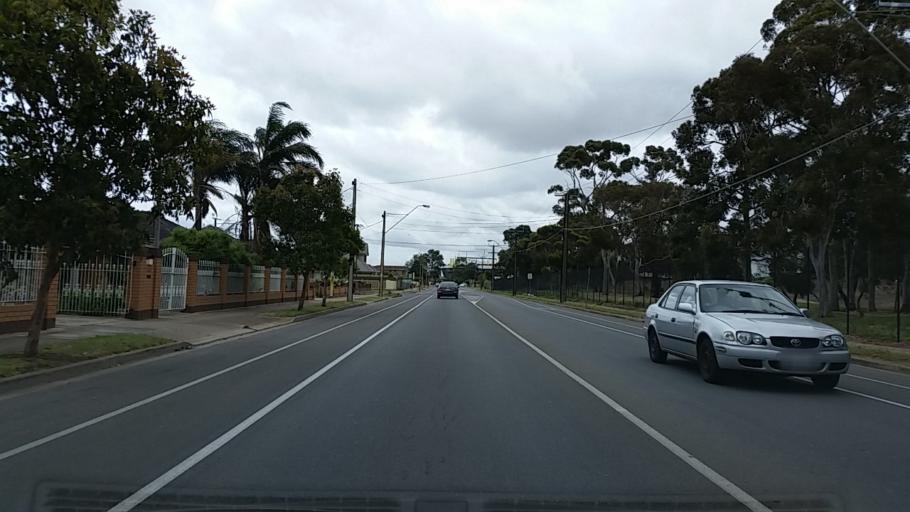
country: AU
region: South Australia
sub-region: Charles Sturt
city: Woodville North
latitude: -34.8625
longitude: 138.5654
